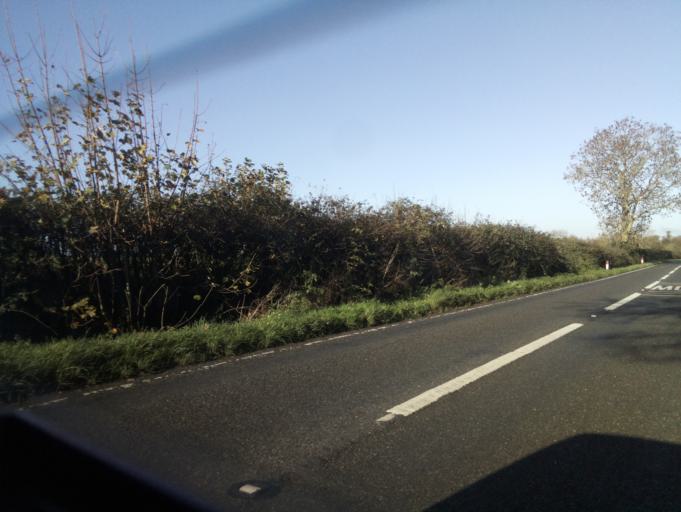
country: GB
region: England
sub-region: Somerset
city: Westonzoyland
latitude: 51.0986
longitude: -2.8946
